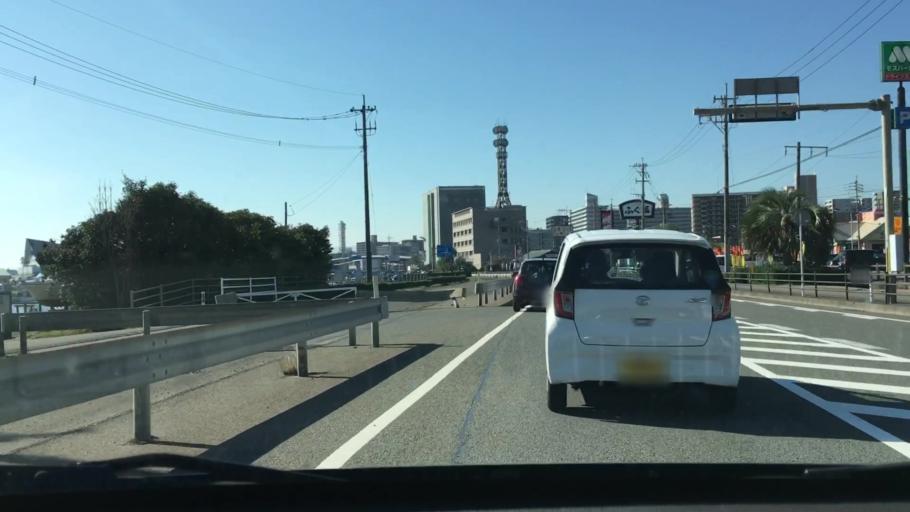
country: JP
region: Kagoshima
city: Kagoshima-shi
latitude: 31.6022
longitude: 130.5666
